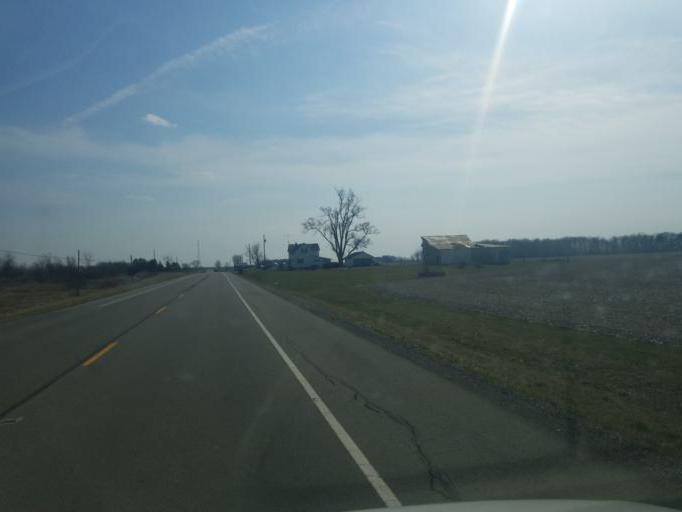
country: US
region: Ohio
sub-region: Logan County
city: Northwood
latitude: 40.5264
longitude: -83.6825
